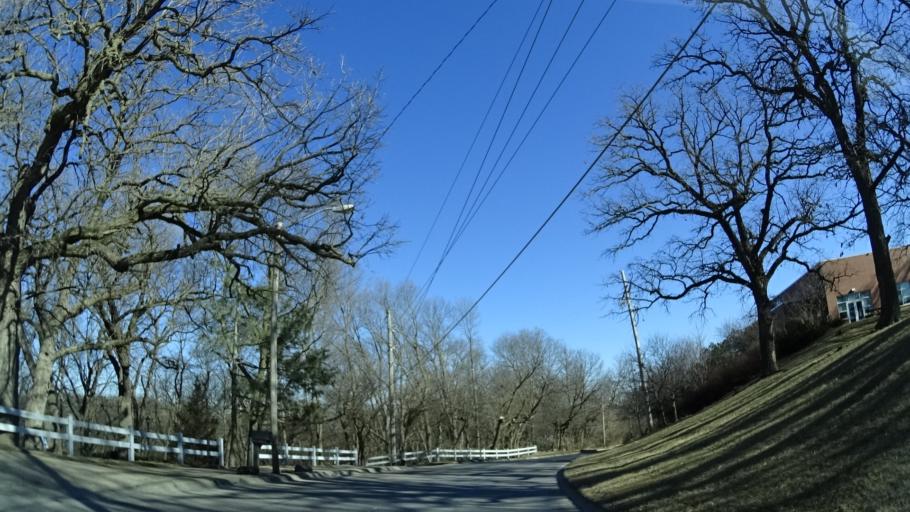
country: US
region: Nebraska
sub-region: Sarpy County
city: Bellevue
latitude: 41.1486
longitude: -95.8979
